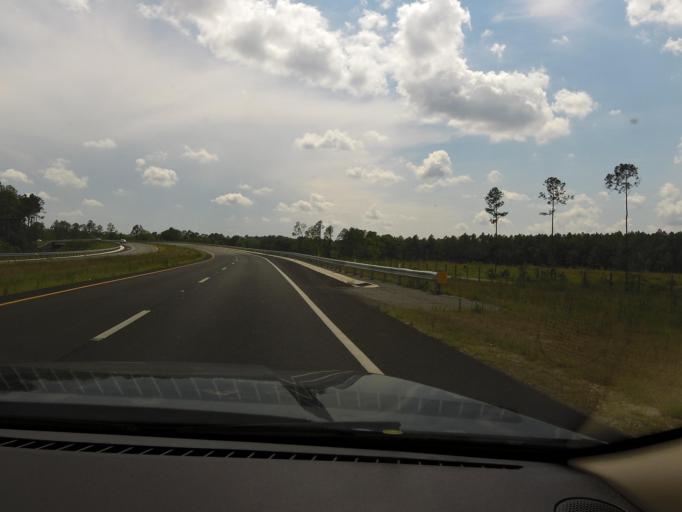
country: US
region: Florida
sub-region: Duval County
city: Baldwin
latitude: 30.3108
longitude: -81.9856
